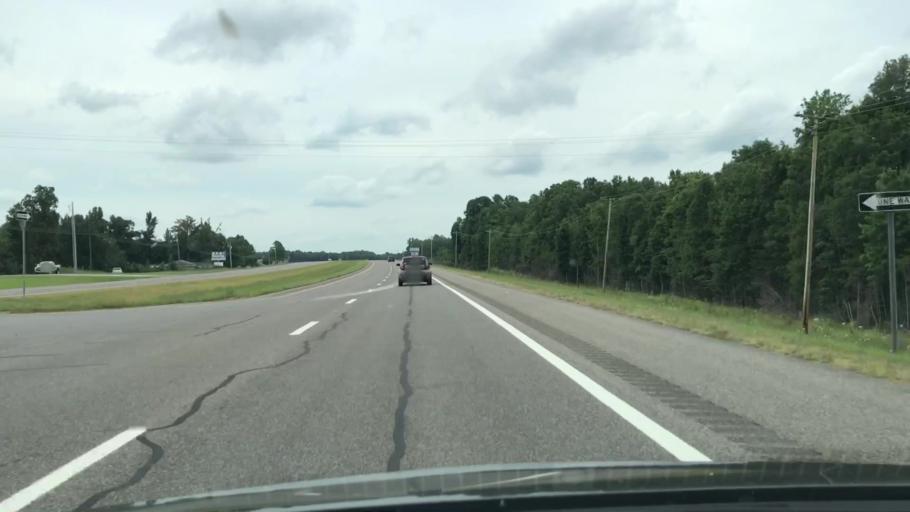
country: US
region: Tennessee
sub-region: Fentress County
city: Jamestown
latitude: 36.3635
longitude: -84.9475
